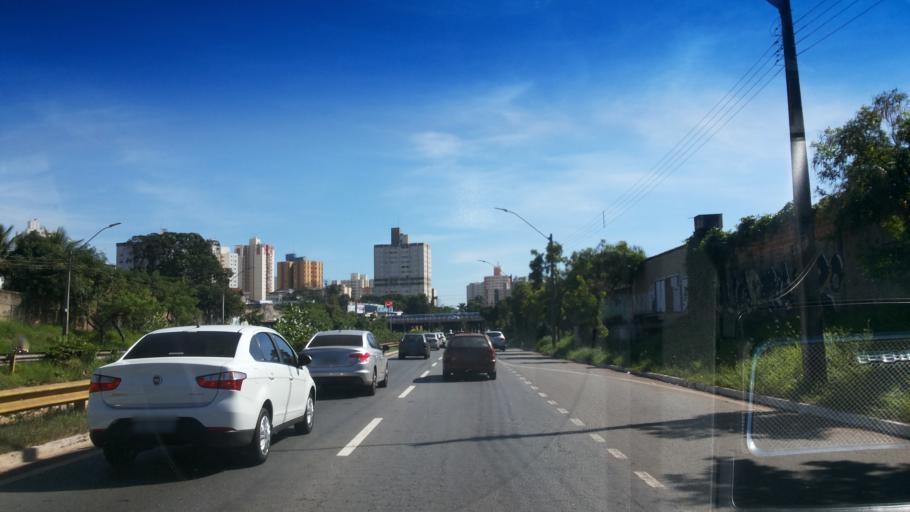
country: BR
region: Goias
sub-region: Goiania
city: Goiania
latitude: -16.6807
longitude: -49.2483
